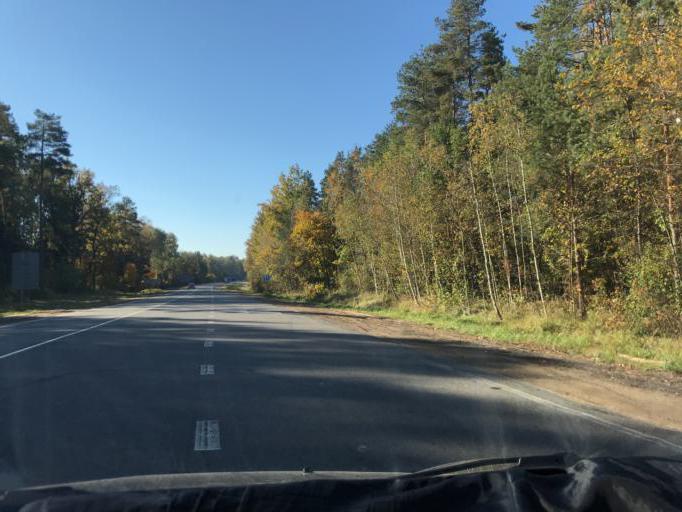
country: BY
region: Mogilev
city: Babruysk
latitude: 53.2052
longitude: 29.0711
